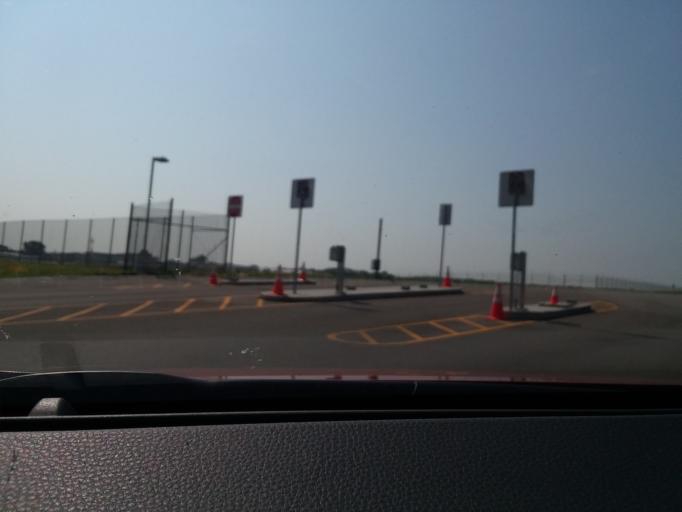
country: US
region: Wisconsin
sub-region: Dane County
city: Maple Bluff
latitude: 43.1316
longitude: -89.3466
